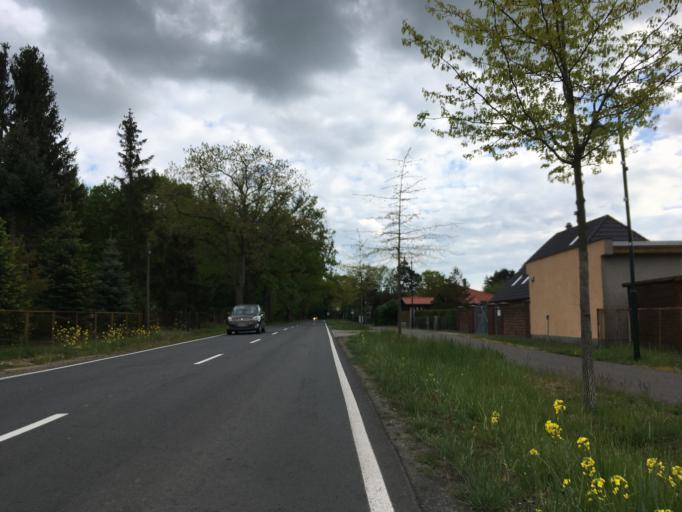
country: DE
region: Brandenburg
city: Bernau bei Berlin
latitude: 52.6324
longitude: 13.6115
